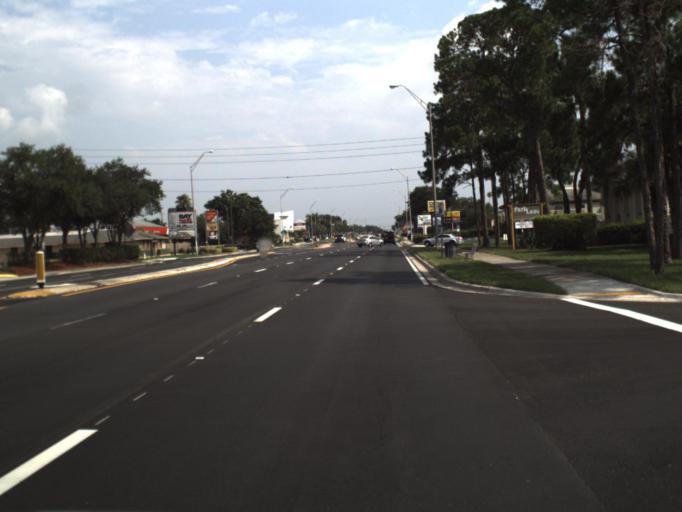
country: US
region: Florida
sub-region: Pinellas County
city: Lealman
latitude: 27.8148
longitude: -82.6385
